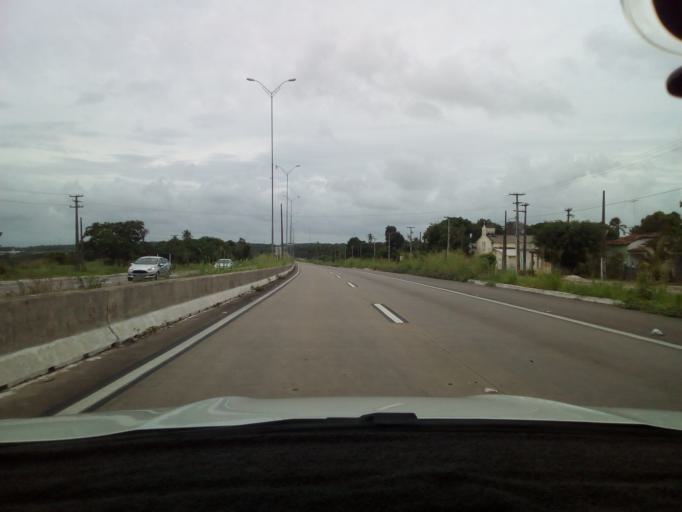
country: BR
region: Paraiba
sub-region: Conde
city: Conde
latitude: -7.3461
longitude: -34.9481
